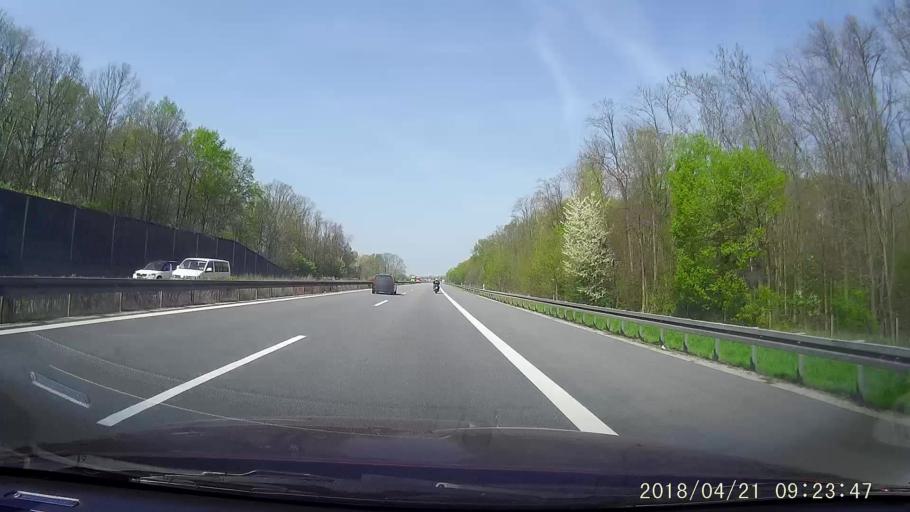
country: DE
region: Saxony
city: Malschwitz
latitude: 51.2064
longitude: 14.5196
